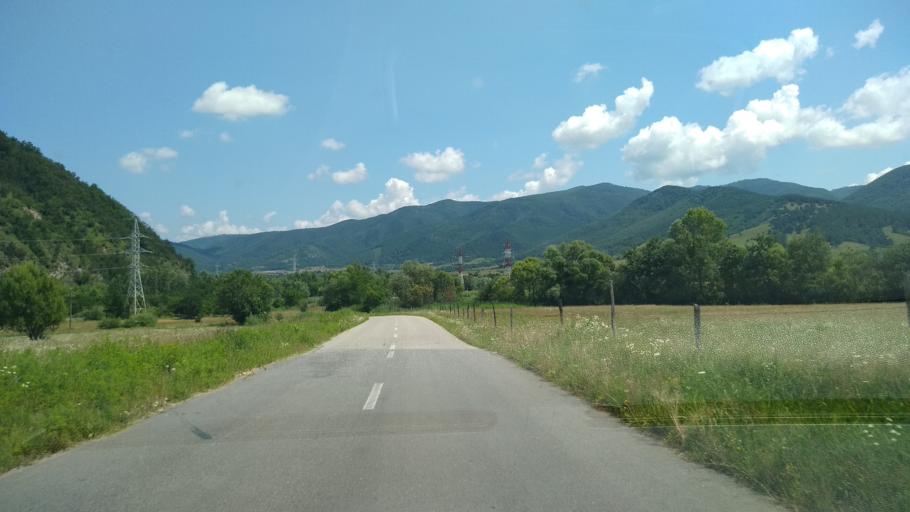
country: RO
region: Hunedoara
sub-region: Comuna Santamaria-Orlea
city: Santamaria-Orlea
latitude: 45.5885
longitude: 22.9826
